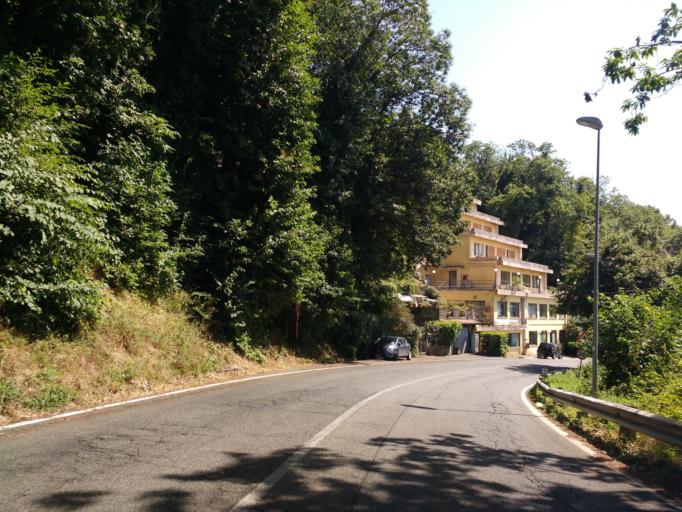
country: IT
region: Latium
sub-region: Citta metropolitana di Roma Capitale
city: Rocca di Papa
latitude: 41.7515
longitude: 12.6999
